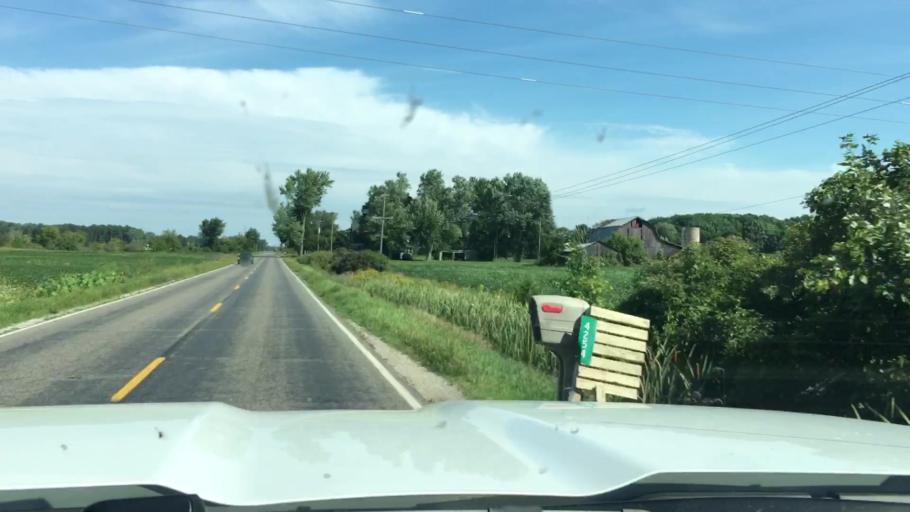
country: US
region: Michigan
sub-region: Saginaw County
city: Hemlock
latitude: 43.4890
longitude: -84.2299
